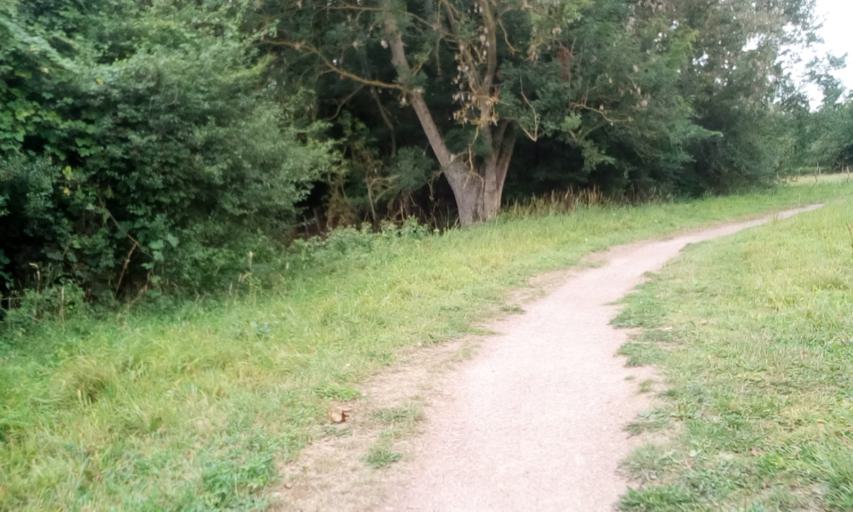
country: FR
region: Lower Normandy
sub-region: Departement du Calvados
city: Eterville
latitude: 49.1590
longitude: -0.4332
